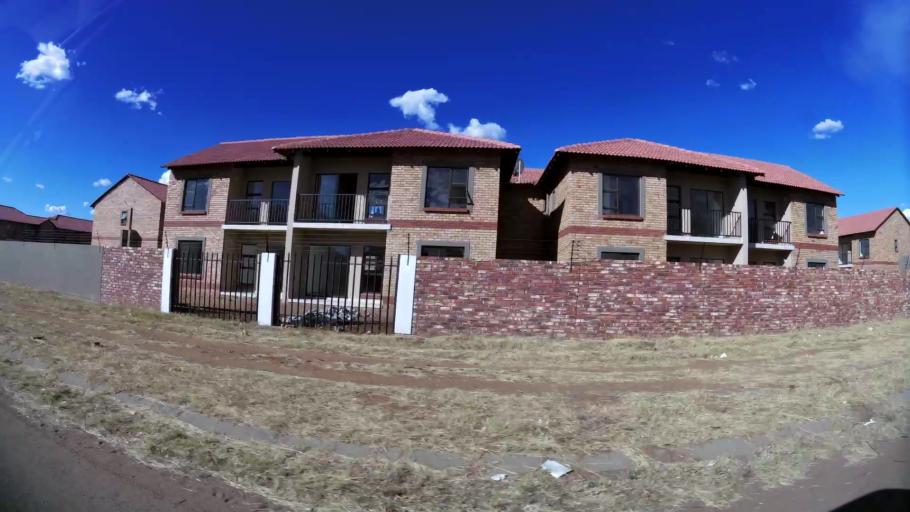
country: ZA
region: North-West
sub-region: Dr Kenneth Kaunda District Municipality
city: Klerksdorp
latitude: -26.8232
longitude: 26.6574
